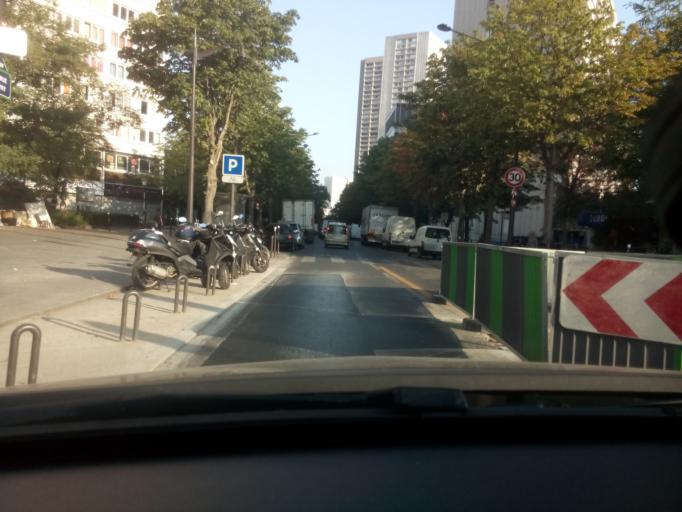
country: FR
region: Ile-de-France
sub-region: Departement du Val-de-Marne
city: Le Kremlin-Bicetre
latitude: 48.8225
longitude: 2.3673
